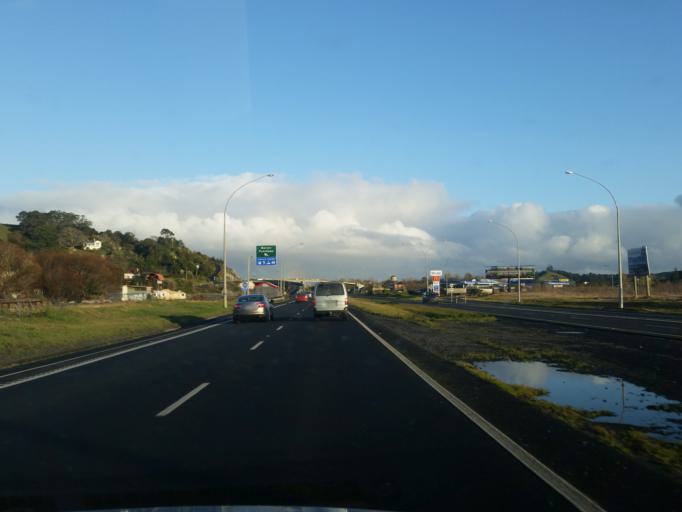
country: NZ
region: Auckland
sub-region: Auckland
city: Pukekohe East
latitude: -37.2749
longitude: 175.0468
